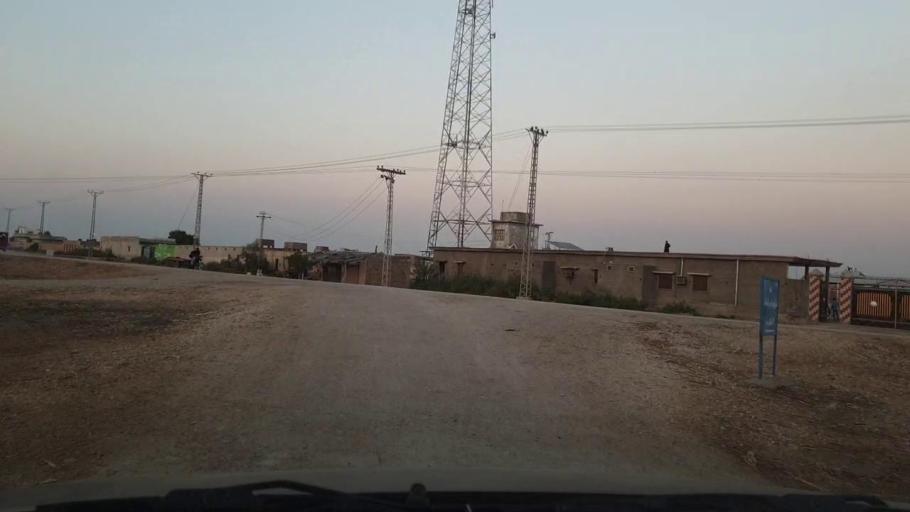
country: PK
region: Sindh
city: Jhol
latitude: 25.9525
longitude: 68.9768
